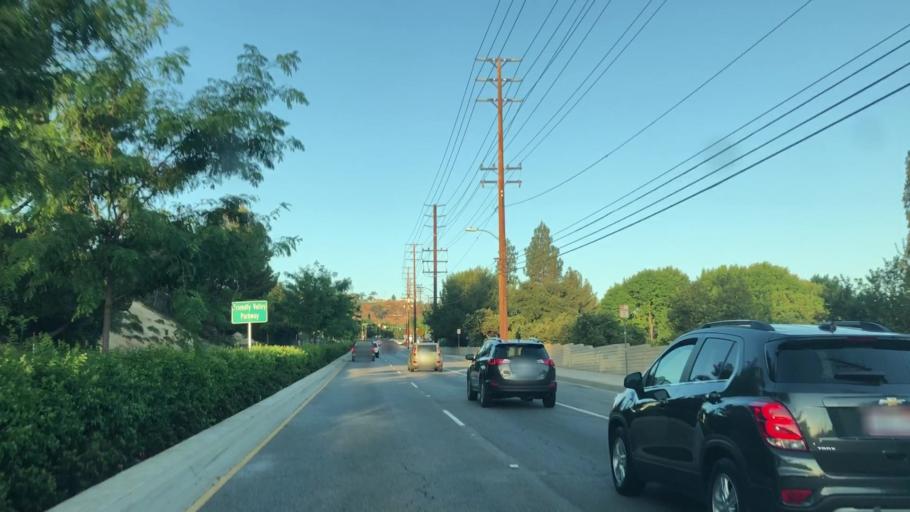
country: US
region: California
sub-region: Los Angeles County
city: Santa Clarita
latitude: 34.4013
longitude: -118.4714
